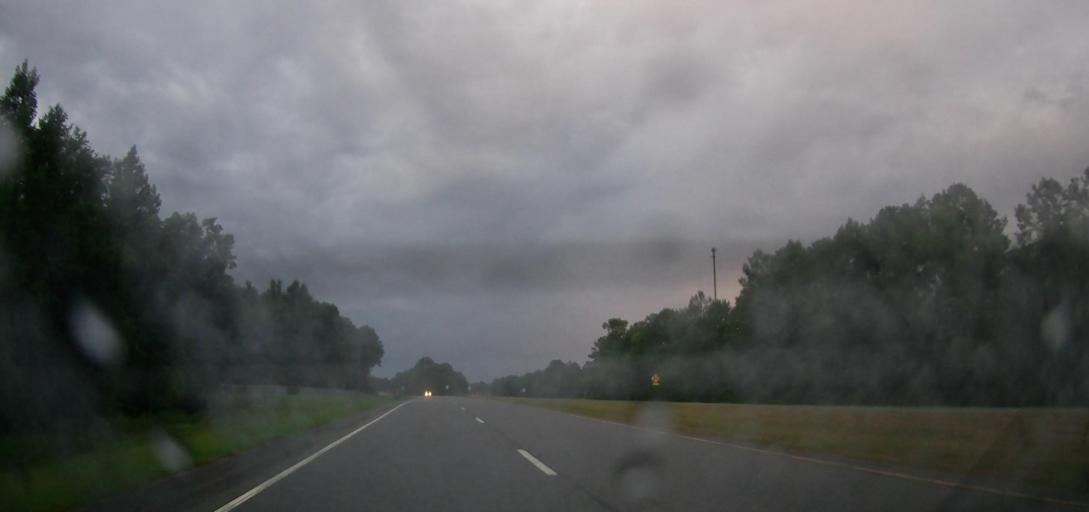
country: US
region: Georgia
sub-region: Lanier County
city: Lakeland
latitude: 30.9328
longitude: -83.0161
